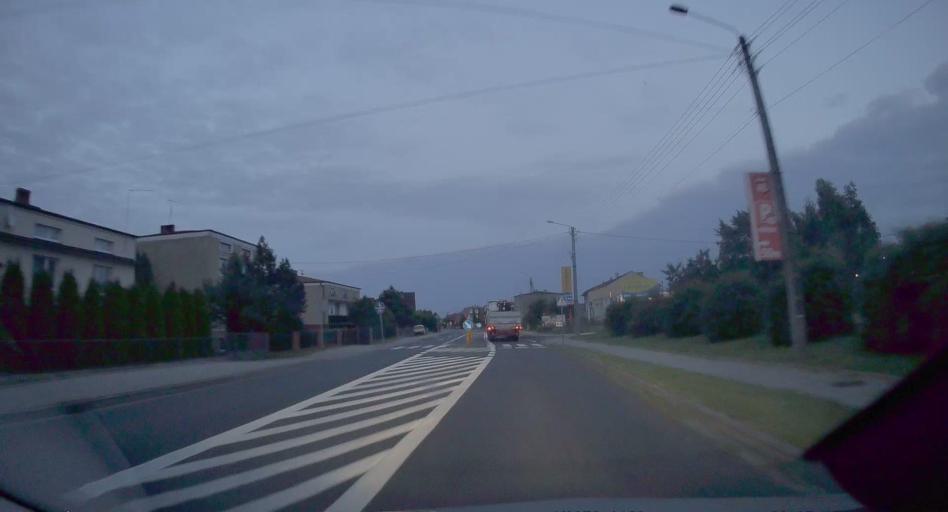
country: PL
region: Silesian Voivodeship
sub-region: Powiat klobucki
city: Opatow
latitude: 50.9284
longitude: 18.8627
